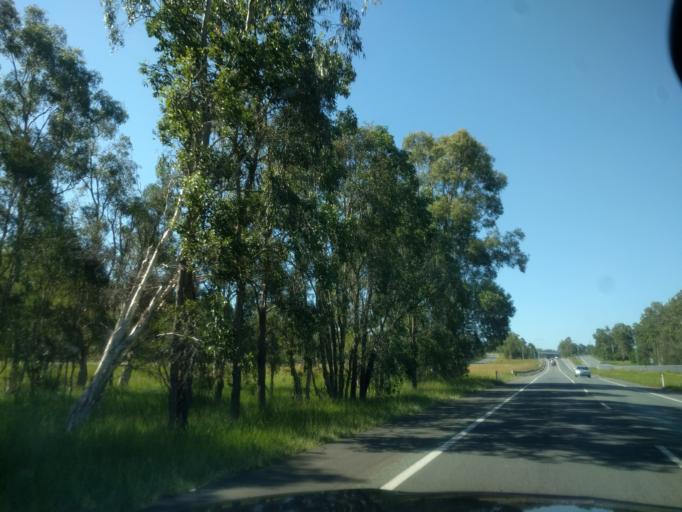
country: AU
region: Queensland
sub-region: Logan
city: Park Ridge South
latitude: -27.7319
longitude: 153.0288
